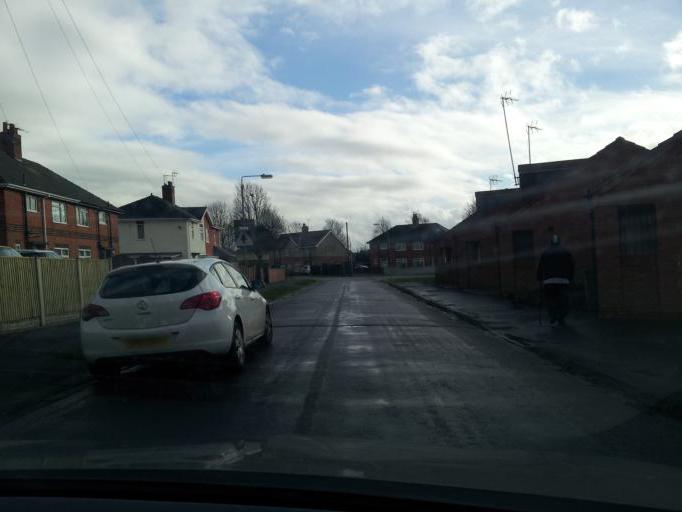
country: GB
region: England
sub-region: Nottinghamshire
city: Newark on Trent
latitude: 53.0648
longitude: -0.8088
